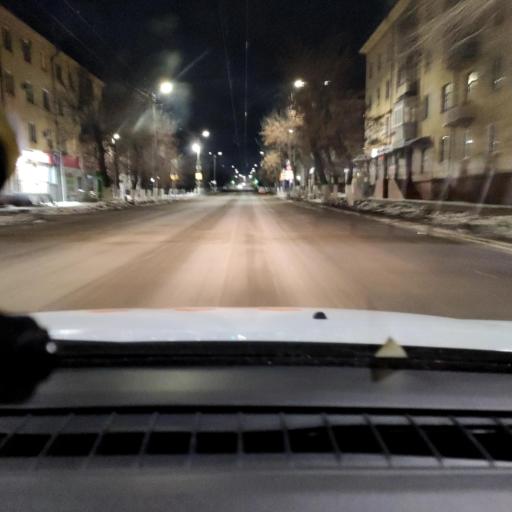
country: RU
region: Samara
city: Novokuybyshevsk
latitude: 53.0937
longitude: 49.9495
